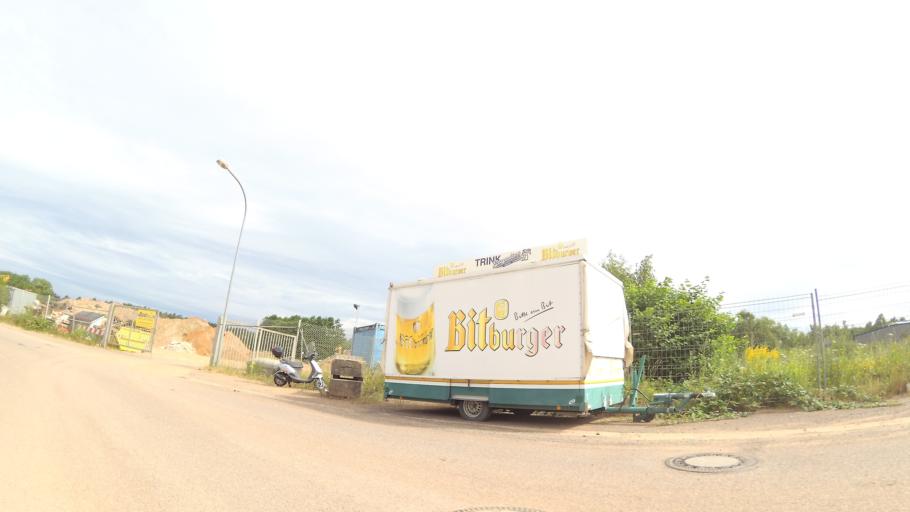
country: DE
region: Saarland
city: Schwalbach
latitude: 49.3260
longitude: 6.8102
